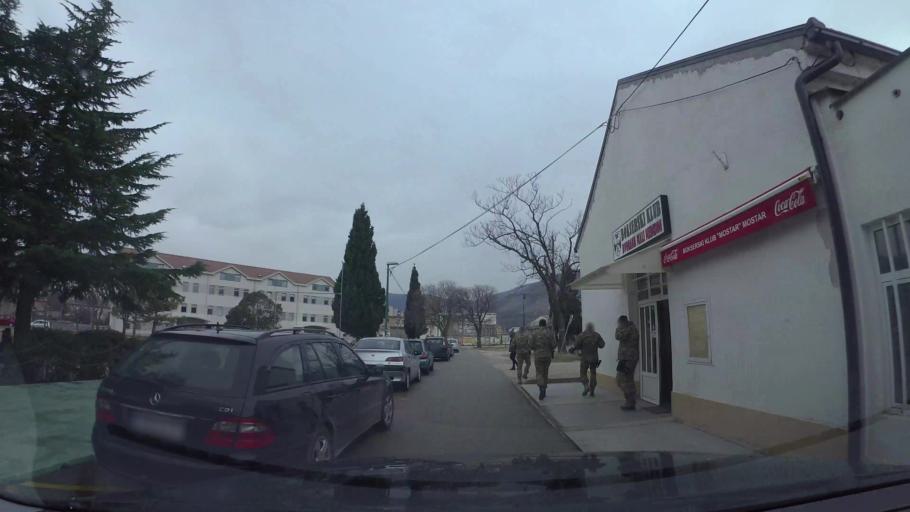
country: BA
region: Federation of Bosnia and Herzegovina
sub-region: Hercegovacko-Bosanski Kanton
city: Mostar
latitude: 43.3538
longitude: 17.8099
